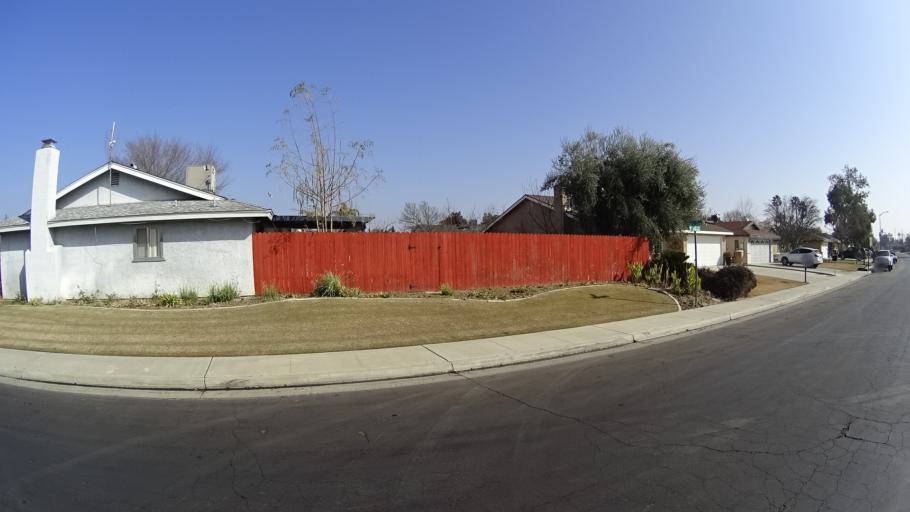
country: US
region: California
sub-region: Kern County
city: Greenacres
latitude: 35.3239
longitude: -119.0716
